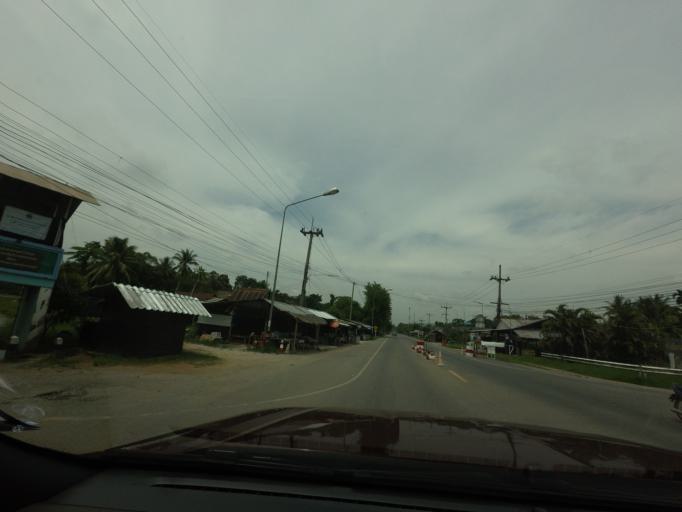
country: TH
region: Pattani
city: Mae Lan
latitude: 6.6846
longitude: 101.2994
